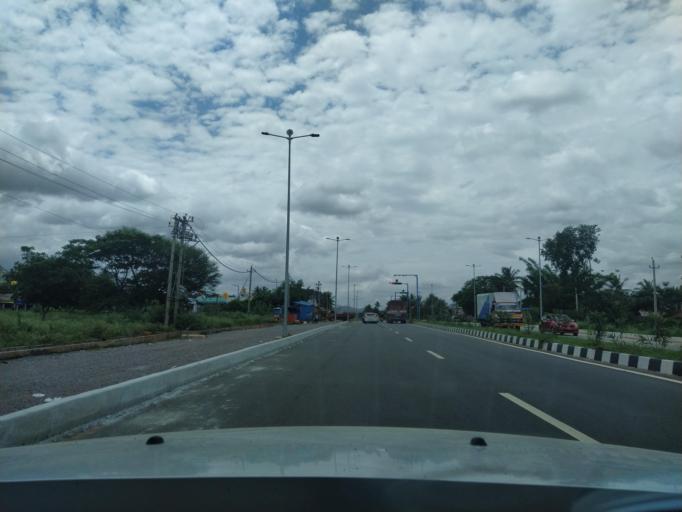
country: IN
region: Karnataka
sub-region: Tumkur
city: Tumkur
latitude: 13.3090
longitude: 77.1416
